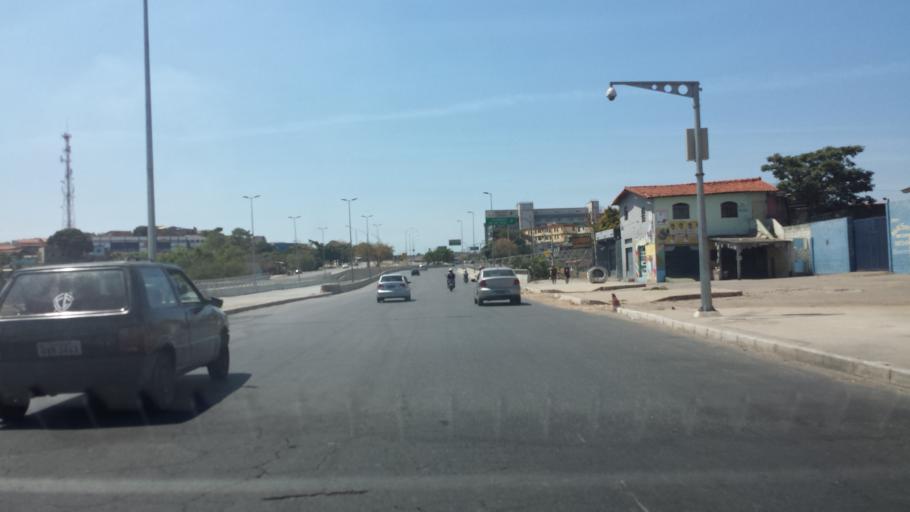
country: BR
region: Minas Gerais
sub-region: Belo Horizonte
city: Belo Horizonte
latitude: -19.8208
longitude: -43.9520
